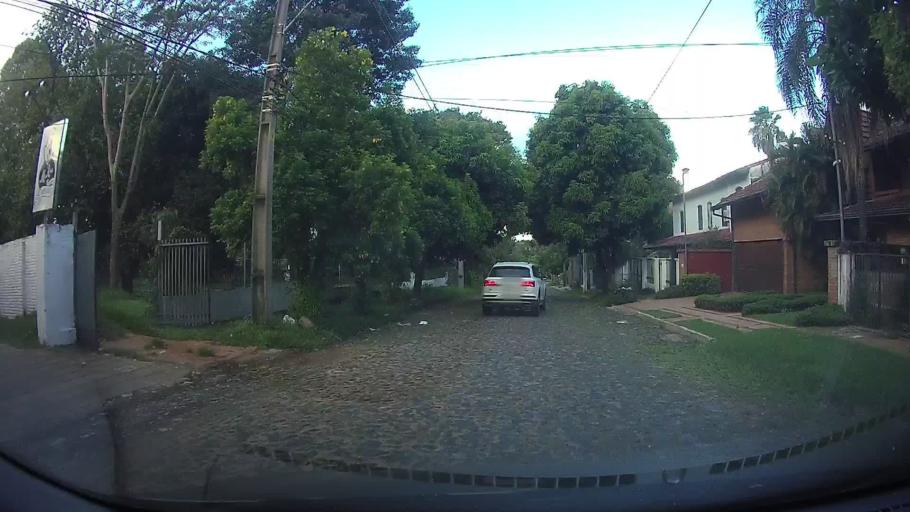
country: PY
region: Asuncion
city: Asuncion
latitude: -25.2793
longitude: -57.5663
